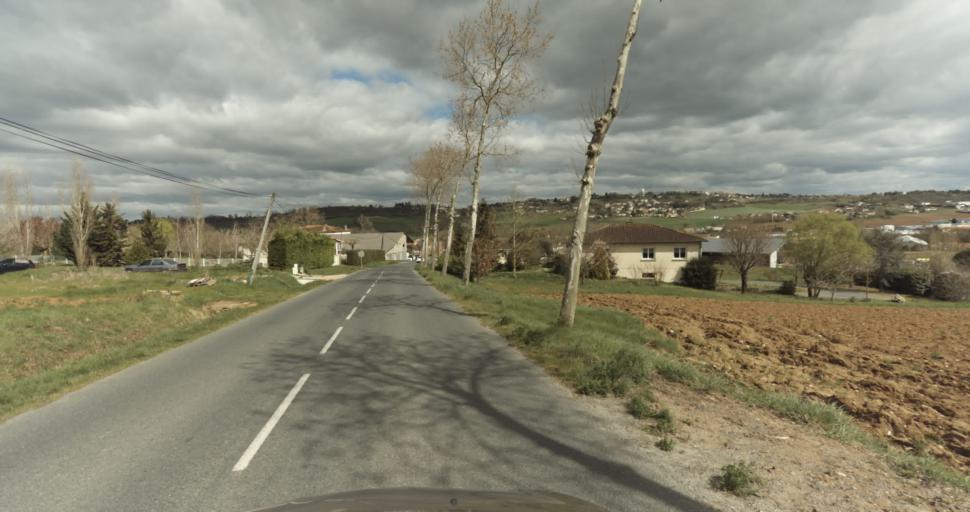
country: FR
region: Midi-Pyrenees
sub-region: Departement du Tarn
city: Puygouzon
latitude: 43.8934
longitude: 2.1479
